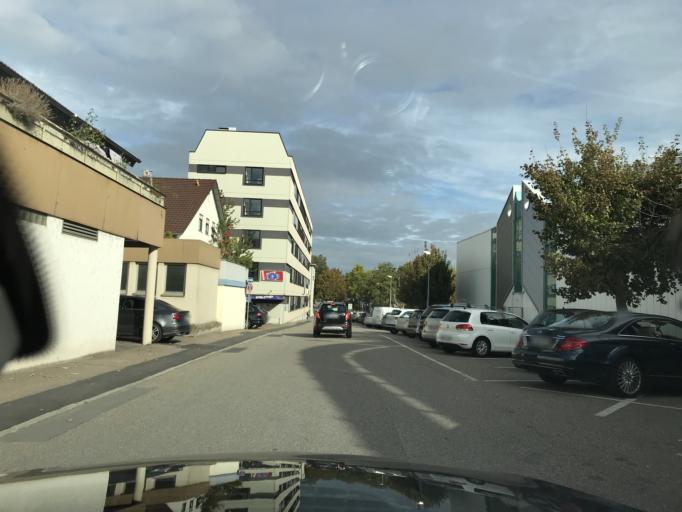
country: DE
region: Baden-Wuerttemberg
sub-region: Regierungsbezirk Stuttgart
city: Waiblingen
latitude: 48.8176
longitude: 9.2994
